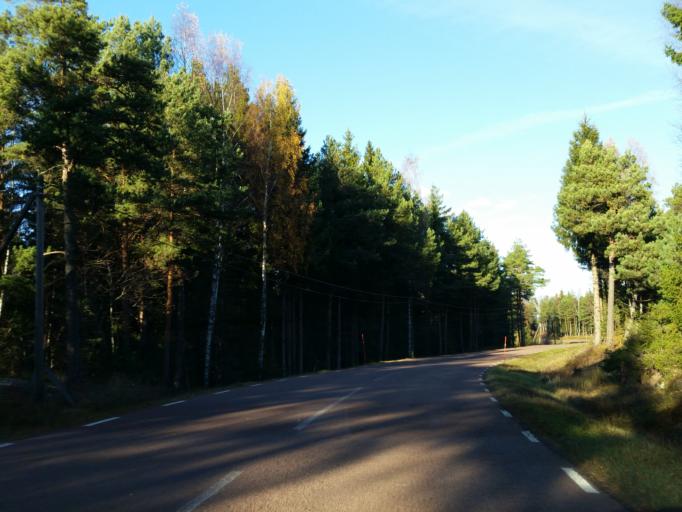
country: AX
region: Alands landsbygd
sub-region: Finstroem
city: Finstroem
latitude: 60.3169
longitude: 19.9410
